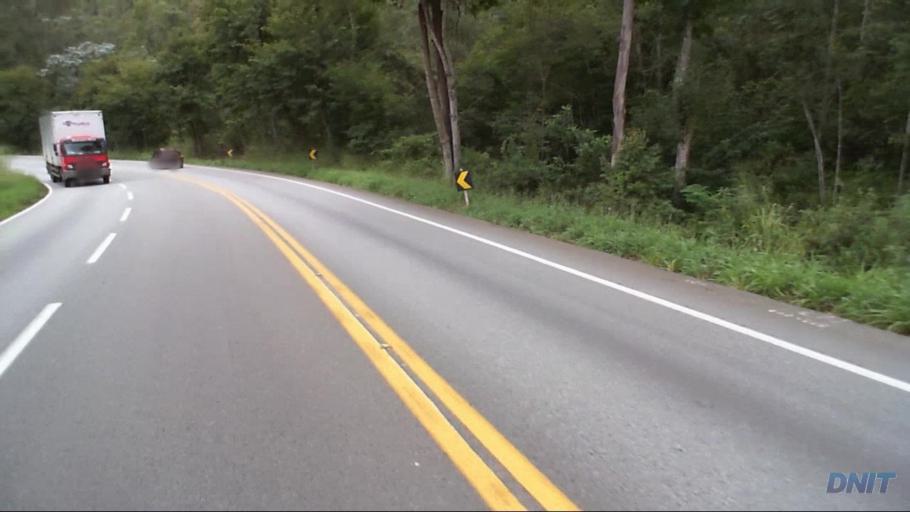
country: BR
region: Minas Gerais
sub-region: Joao Monlevade
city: Joao Monlevade
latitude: -19.8387
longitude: -43.0950
